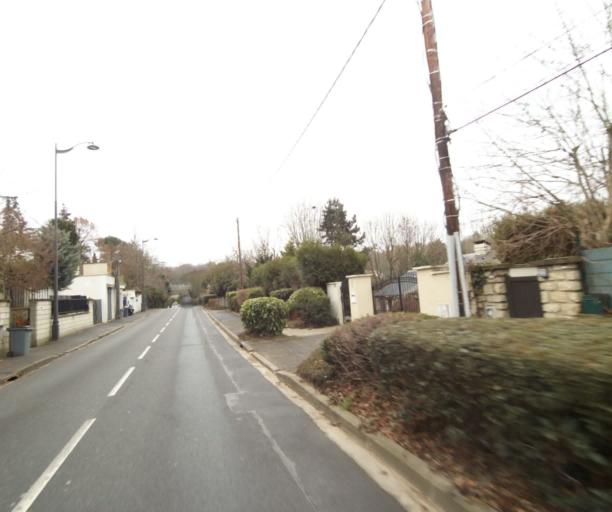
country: FR
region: Ile-de-France
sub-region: Departement des Yvelines
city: La Celle-Saint-Cloud
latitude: 48.8628
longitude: 2.1651
